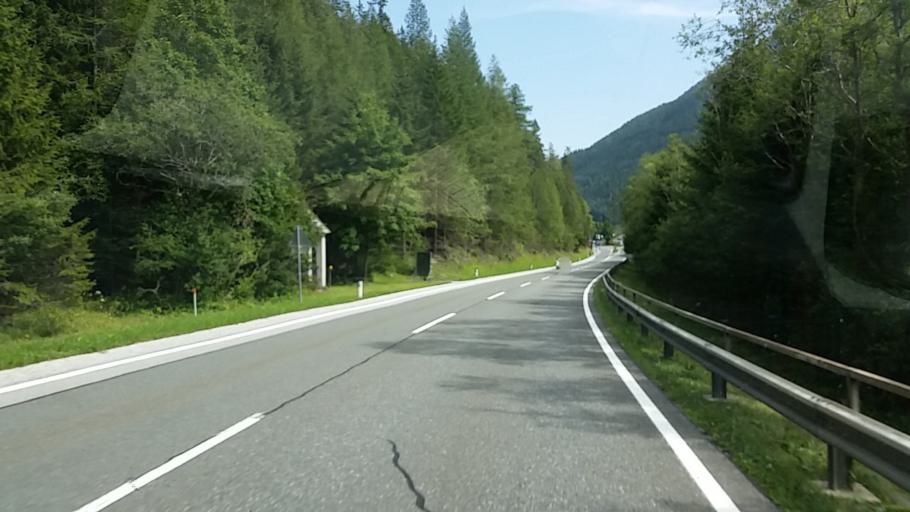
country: AT
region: Salzburg
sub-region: Politischer Bezirk Tamsweg
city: Tweng
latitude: 47.1940
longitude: 13.5956
